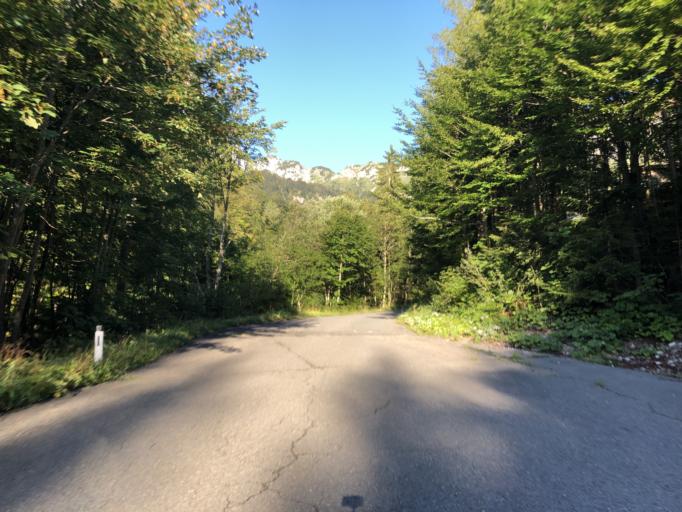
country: AT
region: Tyrol
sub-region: Politischer Bezirk Kufstein
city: Ellmau
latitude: 47.5795
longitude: 12.3316
